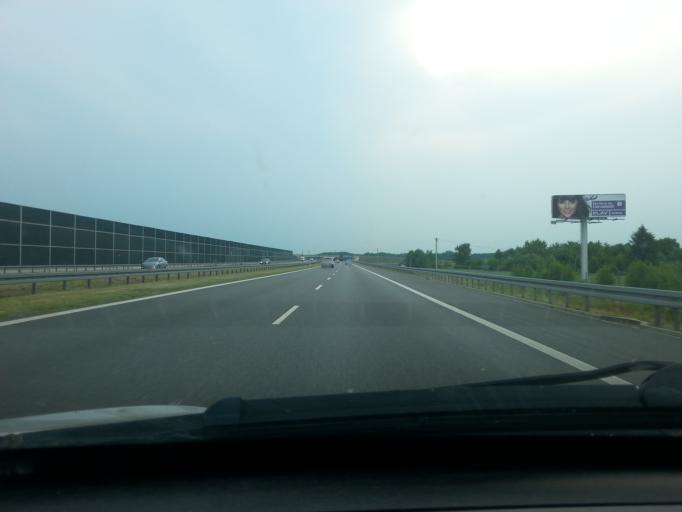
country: PL
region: Lodz Voivodeship
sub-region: Powiat skierniewicki
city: Bolimow
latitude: 52.0750
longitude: 20.2509
